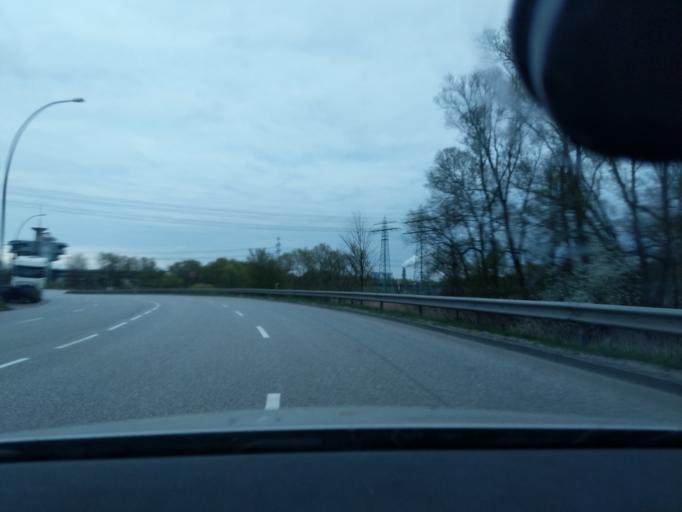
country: DE
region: Hamburg
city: Altona
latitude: 53.5029
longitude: 9.9036
